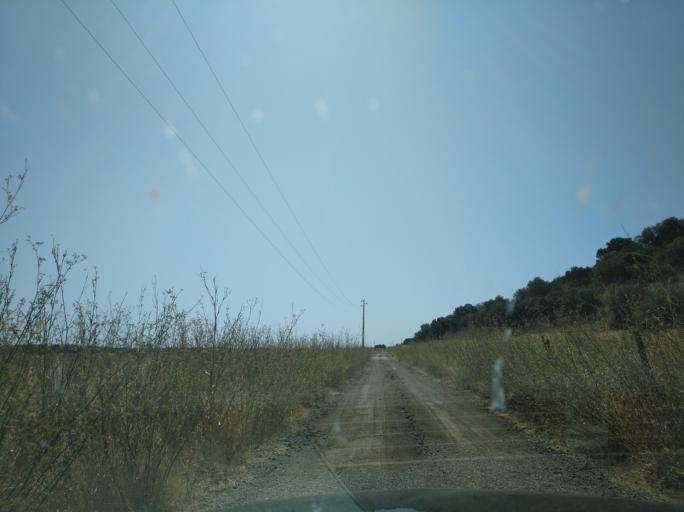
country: PT
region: Portalegre
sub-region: Campo Maior
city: Campo Maior
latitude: 39.0566
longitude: -7.0045
